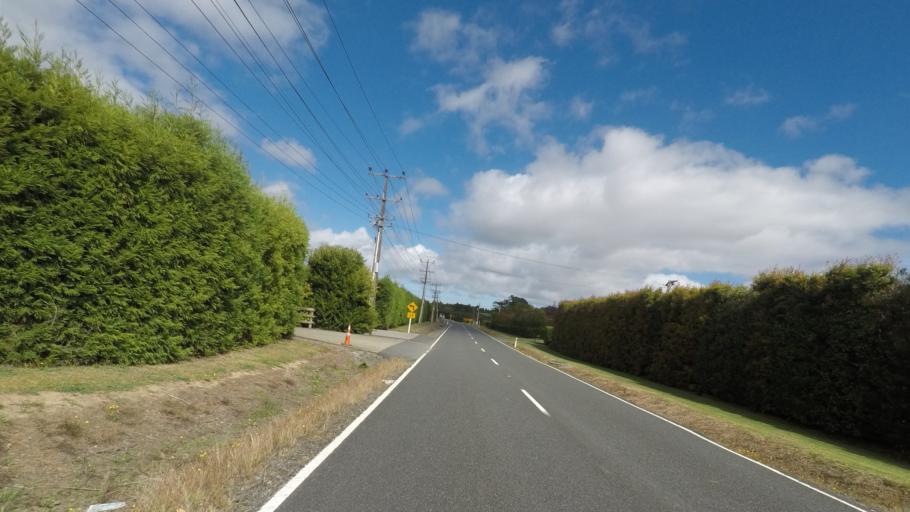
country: NZ
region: Auckland
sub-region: Auckland
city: Muriwai Beach
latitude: -36.7643
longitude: 174.5589
